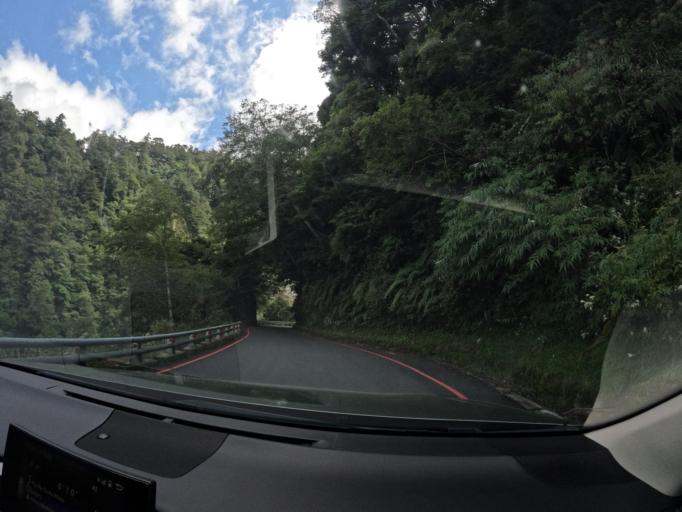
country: TW
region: Taiwan
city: Yujing
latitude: 23.2603
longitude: 120.9191
